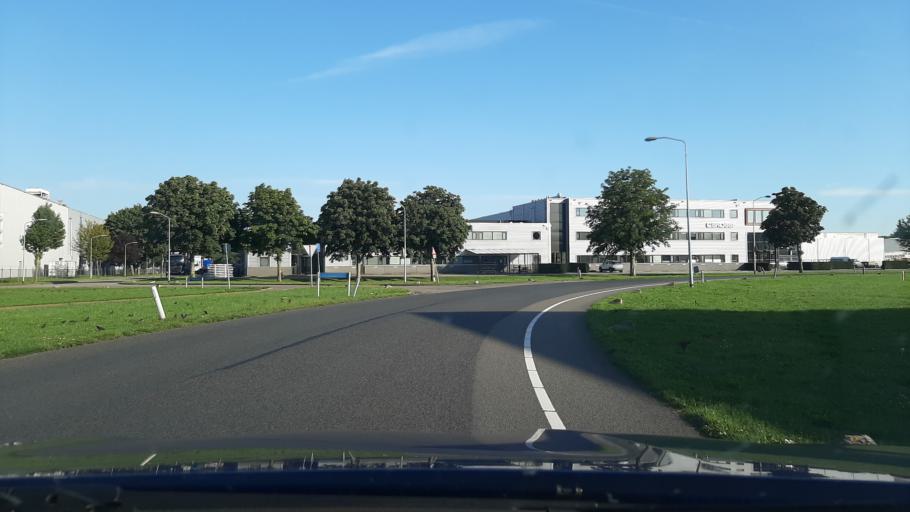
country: NL
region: Flevoland
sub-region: Gemeente Zeewolde
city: Zeewolde
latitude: 52.3573
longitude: 5.5093
